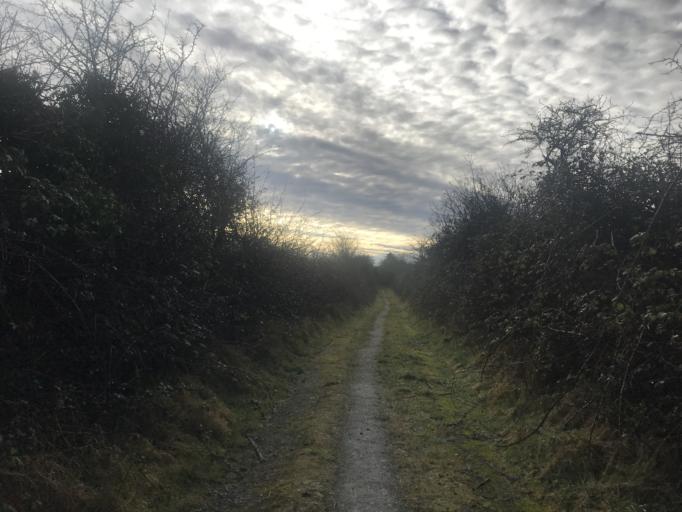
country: IE
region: Connaught
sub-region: County Galway
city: Gaillimh
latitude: 53.3163
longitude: -9.0044
